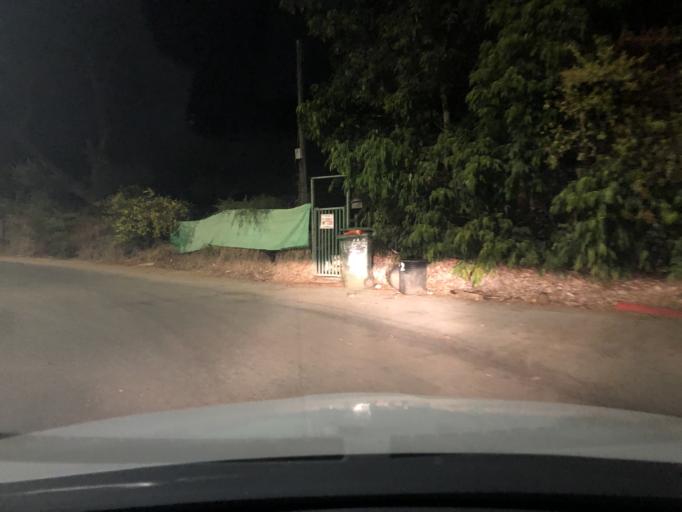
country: IL
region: Central District
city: Hod HaSharon
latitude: 32.1628
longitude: 34.8961
